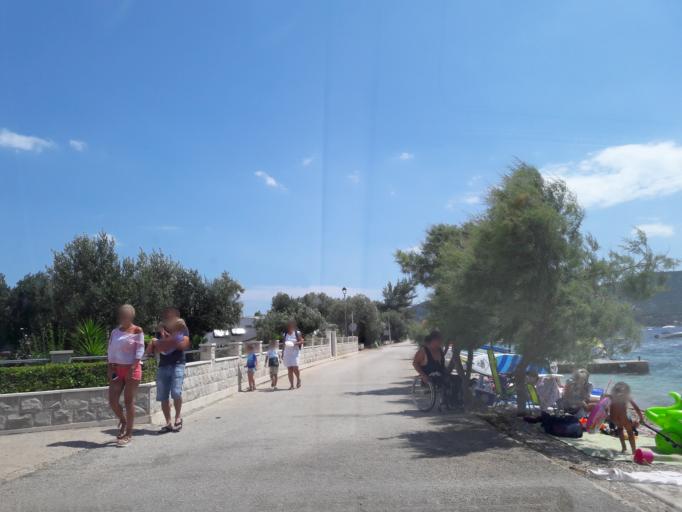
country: HR
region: Dubrovacko-Neretvanska
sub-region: Grad Korcula
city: Zrnovo
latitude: 42.9810
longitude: 17.1027
